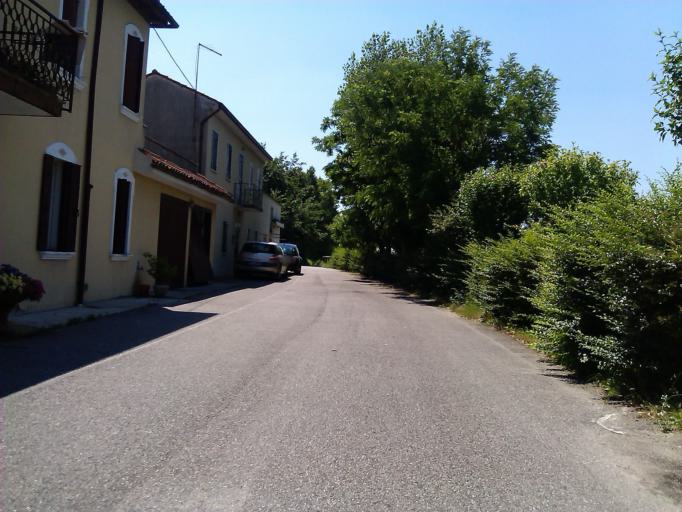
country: IT
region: Veneto
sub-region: Provincia di Treviso
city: Castelfranco Veneto
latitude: 45.6671
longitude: 11.9218
